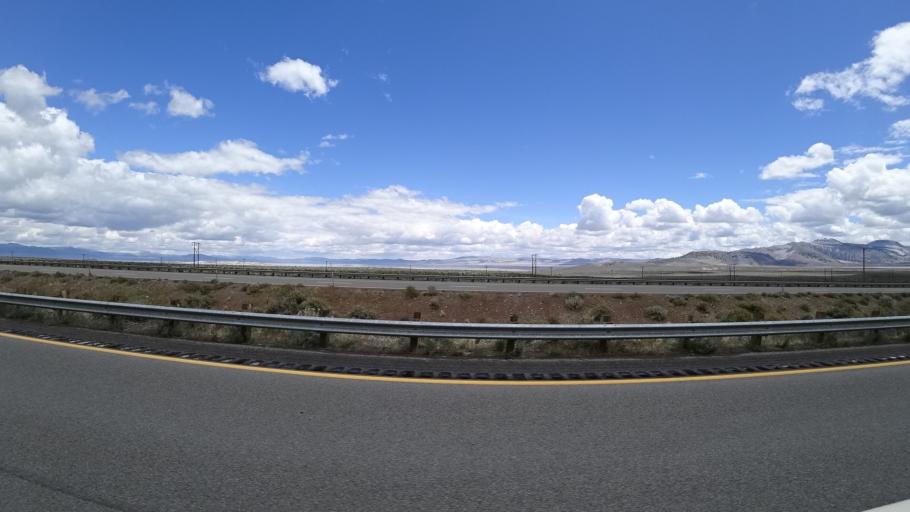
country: US
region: California
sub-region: Mono County
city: Mammoth Lakes
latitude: 37.9404
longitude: -119.1024
